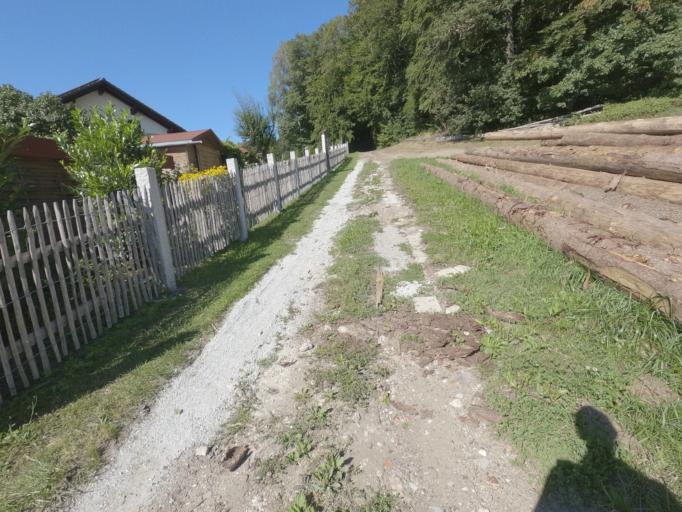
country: DE
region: Bavaria
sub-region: Lower Bavaria
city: Schaufling
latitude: 48.8228
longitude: 13.0213
